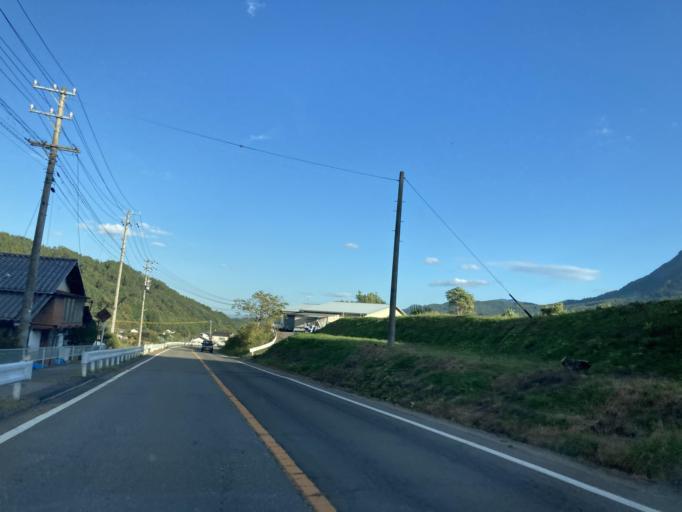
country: JP
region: Nagano
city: Kamimaruko
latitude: 36.3739
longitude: 138.1134
